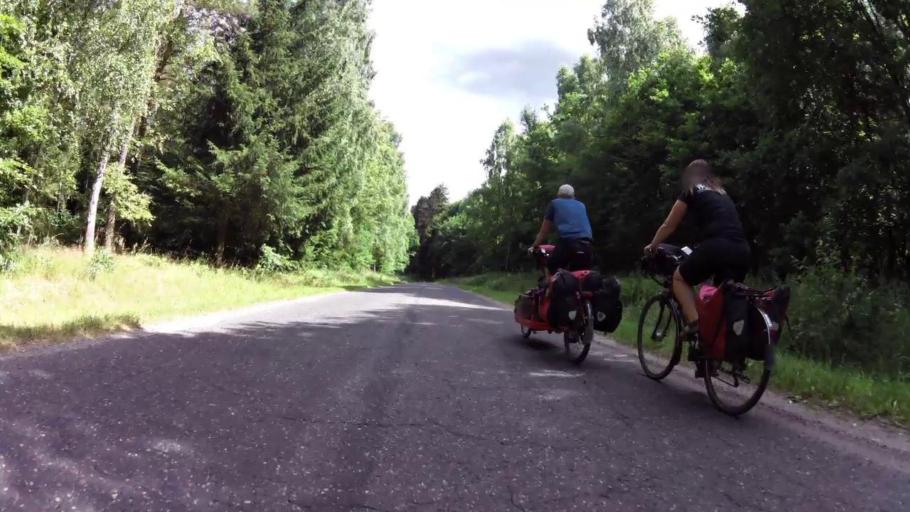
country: PL
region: West Pomeranian Voivodeship
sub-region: Powiat lobeski
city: Lobez
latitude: 53.6617
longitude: 15.5548
